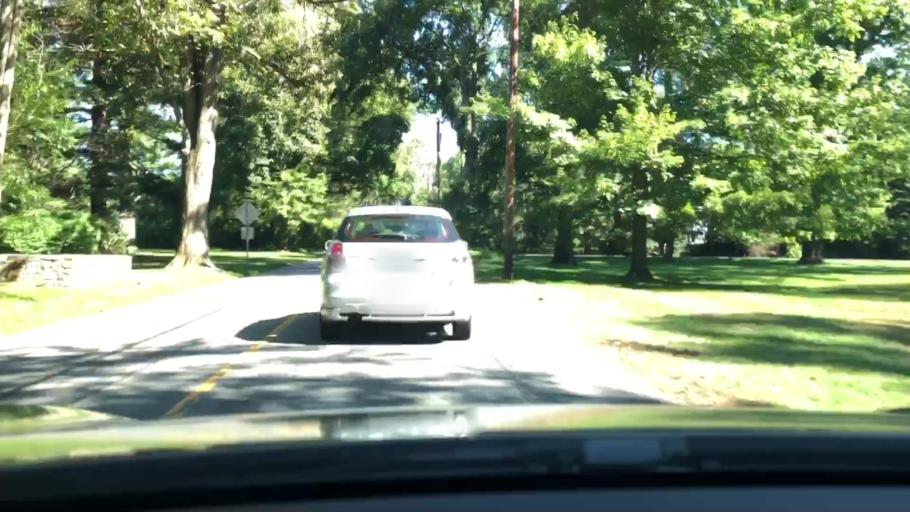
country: US
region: Connecticut
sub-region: Fairfield County
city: Darien
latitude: 41.1121
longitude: -73.4815
